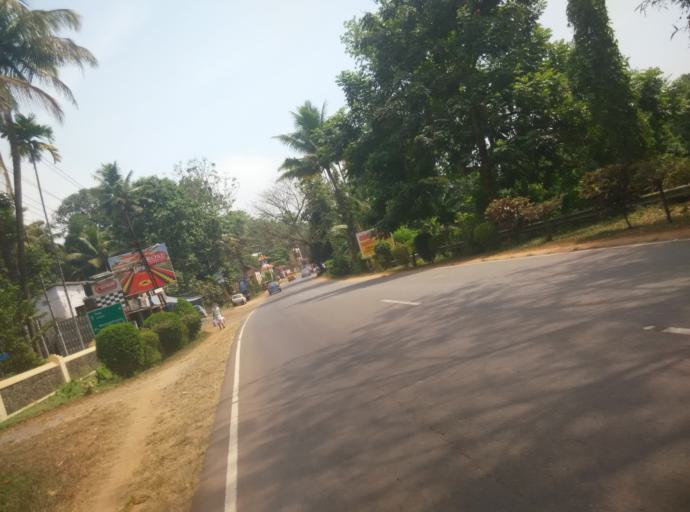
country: IN
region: Kerala
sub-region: Kottayam
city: Palackattumala
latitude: 9.6983
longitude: 76.6498
